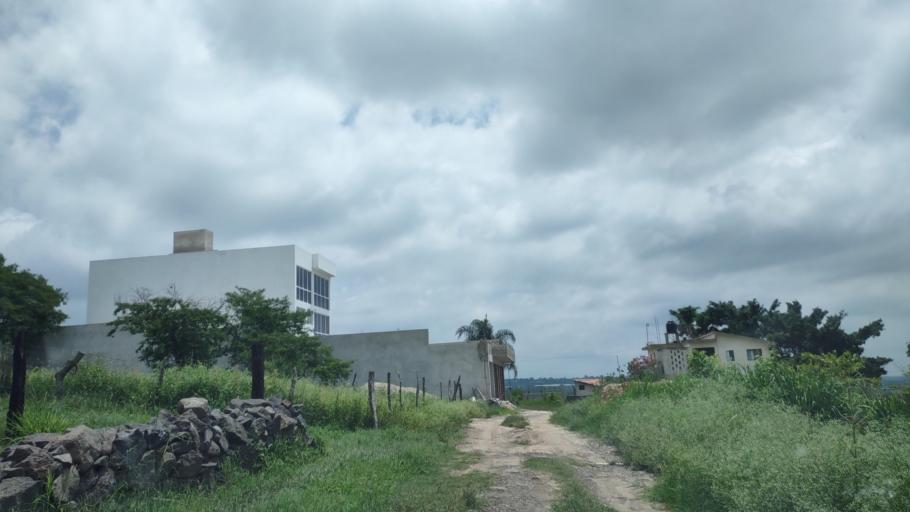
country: MX
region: Veracruz
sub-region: Emiliano Zapata
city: Dos Rios
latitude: 19.4869
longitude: -96.8131
